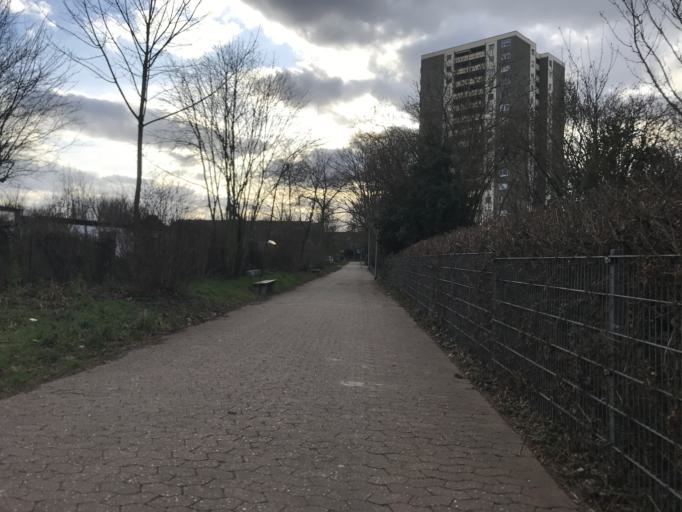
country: DE
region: Rheinland-Pfalz
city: Mainz
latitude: 49.9722
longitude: 8.2464
